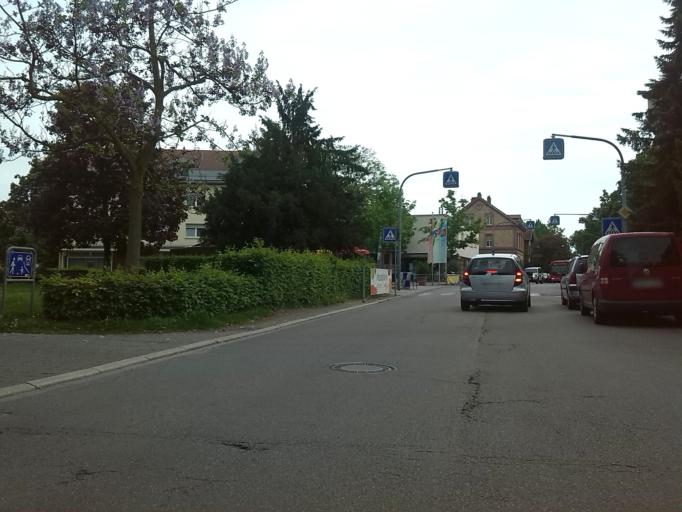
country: DE
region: Baden-Wuerttemberg
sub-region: Karlsruhe Region
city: Ladenburg
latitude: 49.4715
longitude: 8.6068
